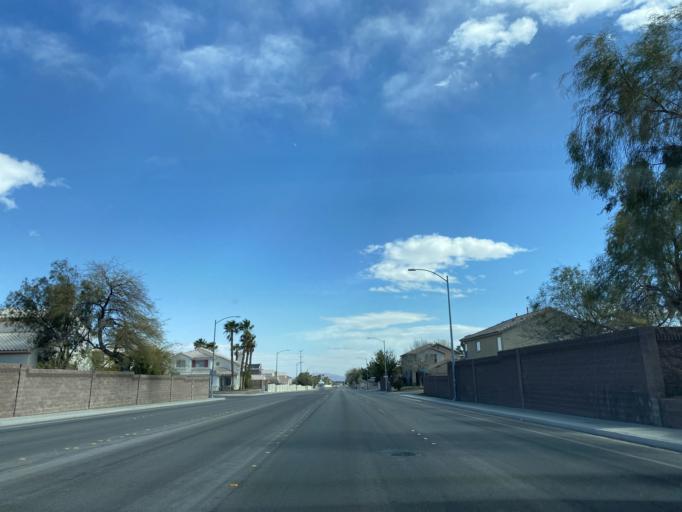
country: US
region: Nevada
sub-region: Clark County
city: Summerlin South
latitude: 36.2261
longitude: -115.2758
